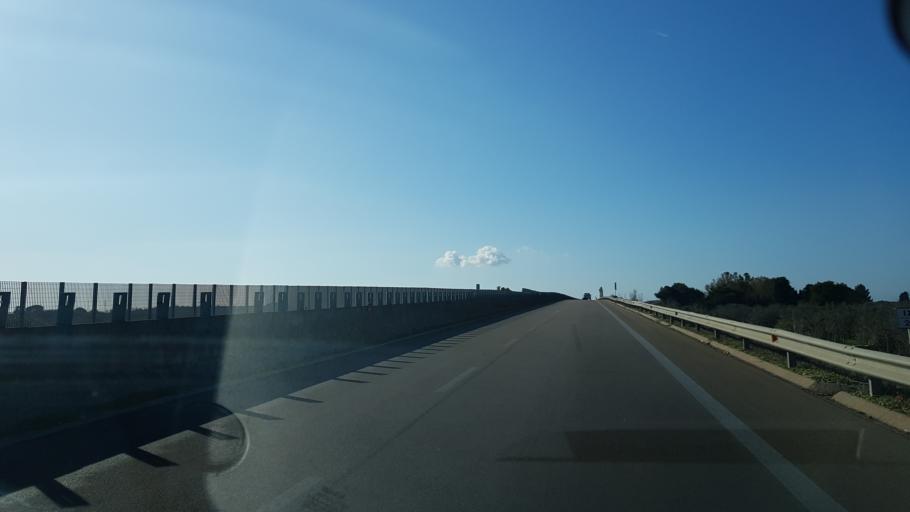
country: IT
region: Apulia
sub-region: Provincia di Lecce
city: Sannicola
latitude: 40.1176
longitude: 18.0455
